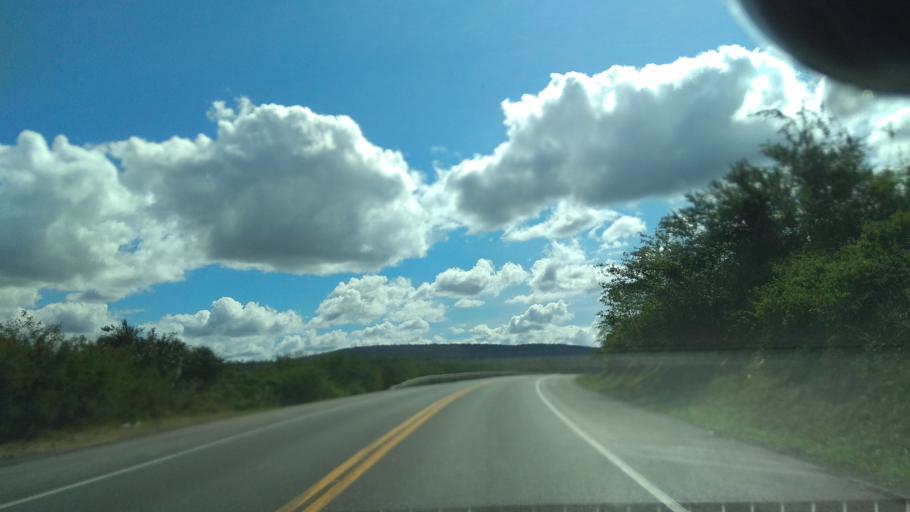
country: BR
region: Bahia
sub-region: Santa Ines
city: Santa Ines
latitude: -13.3100
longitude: -40.0242
